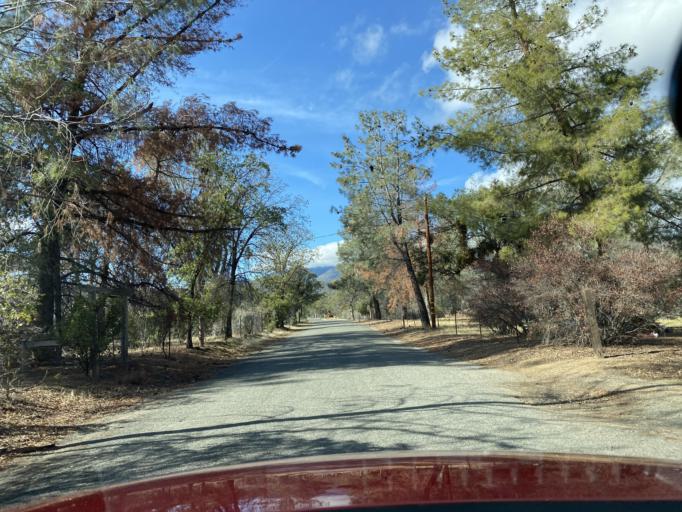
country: US
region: California
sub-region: Lake County
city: Lucerne
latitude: 39.3702
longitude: -122.5838
